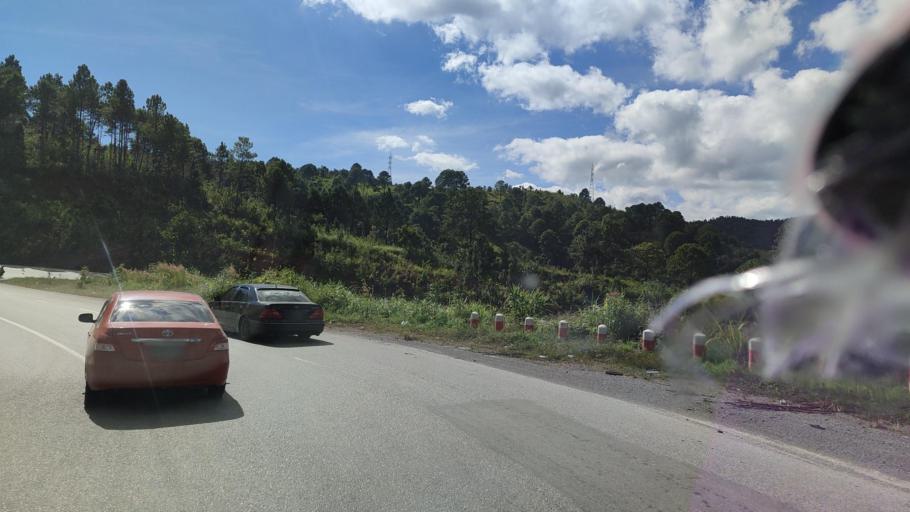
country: MM
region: Mandalay
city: Yamethin
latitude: 20.6566
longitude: 96.5464
